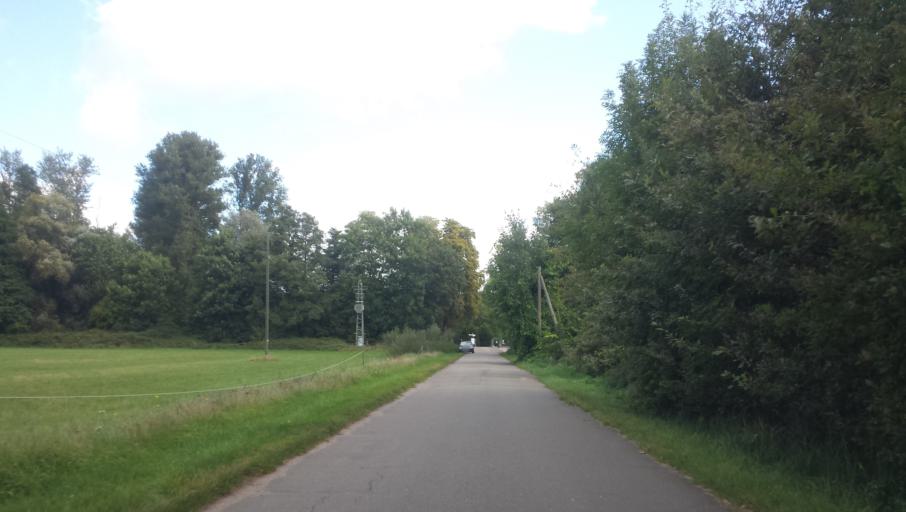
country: DE
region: Rheinland-Pfalz
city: Knittelsheim
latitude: 49.1991
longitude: 8.2576
